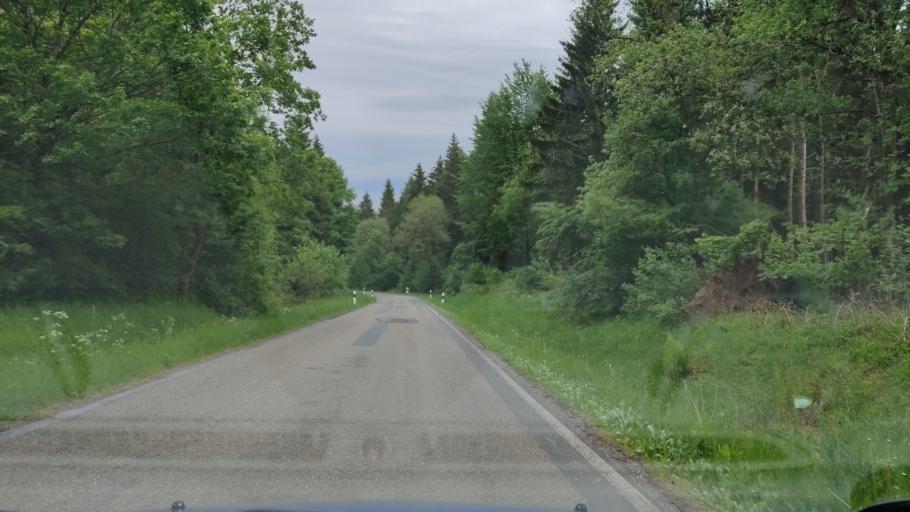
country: DE
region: Lower Saxony
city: Hardegsen
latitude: 51.7090
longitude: 9.7593
